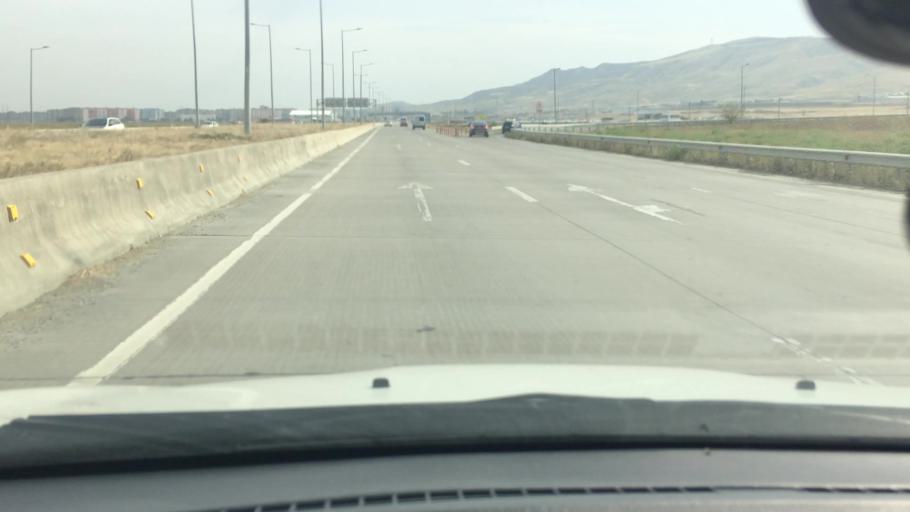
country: GE
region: Kvemo Kartli
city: Rust'avi
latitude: 41.5871
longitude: 44.9492
